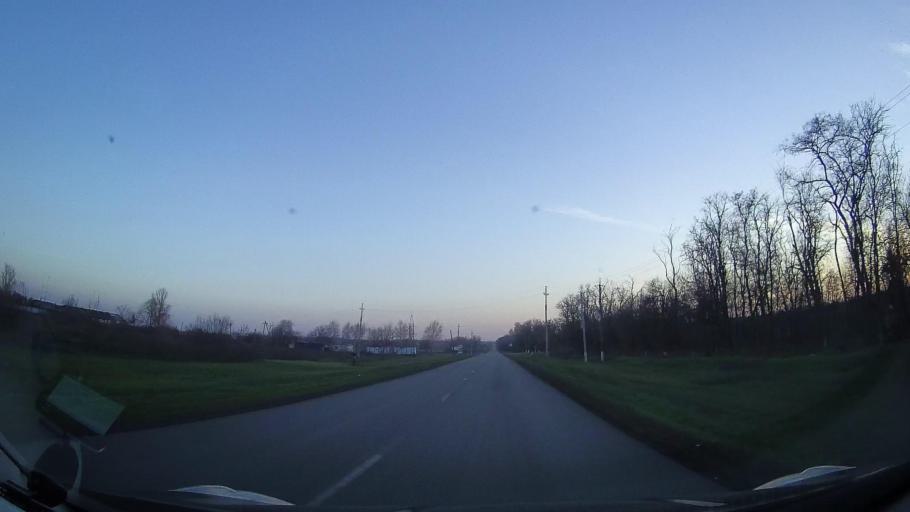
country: RU
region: Rostov
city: Zernograd
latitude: 47.0465
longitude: 40.3915
